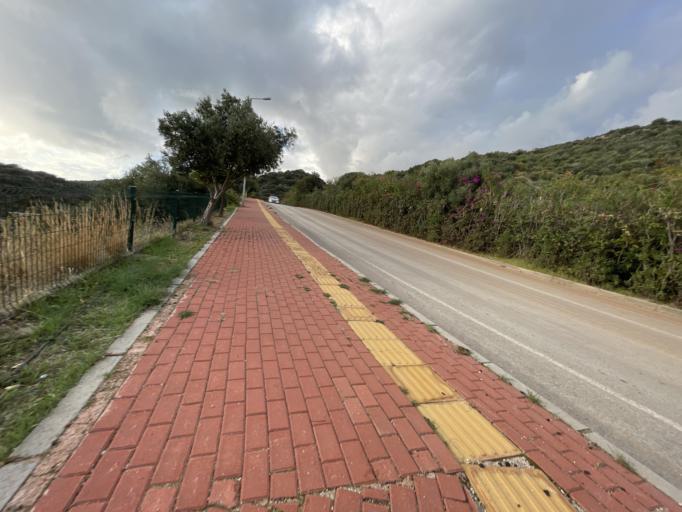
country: TR
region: Antalya
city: Kas
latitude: 36.1992
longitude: 29.6194
